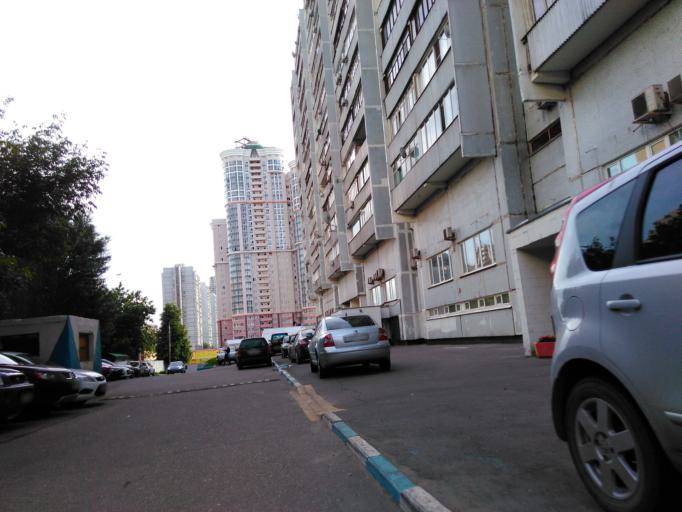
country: RU
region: Moscow
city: Troparevo
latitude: 55.6678
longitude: 37.5176
